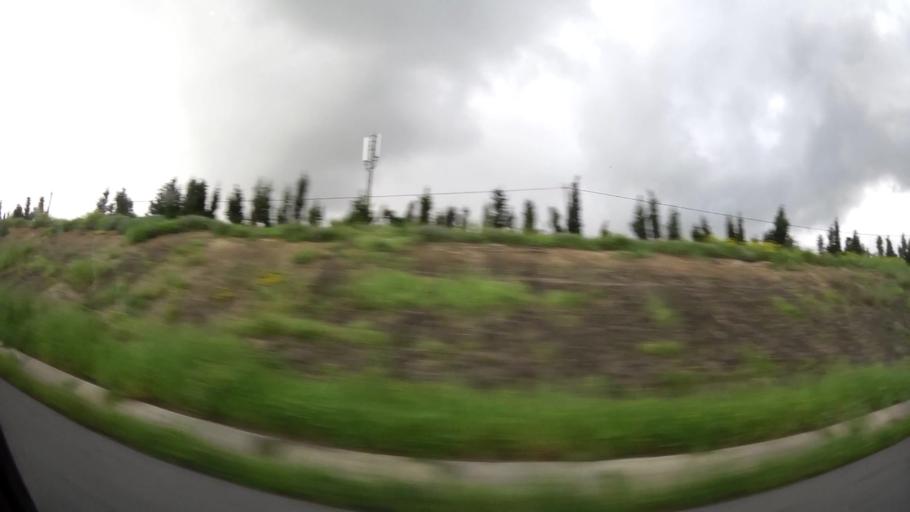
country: MA
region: Grand Casablanca
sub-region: Mediouna
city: Tit Mellil
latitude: 33.5760
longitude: -7.4544
